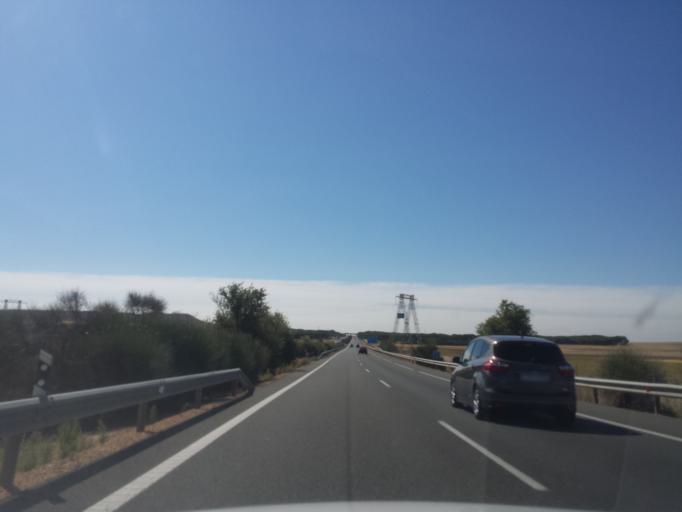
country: ES
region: Castille and Leon
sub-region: Provincia de Valladolid
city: Bercero
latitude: 41.5548
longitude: -5.0797
